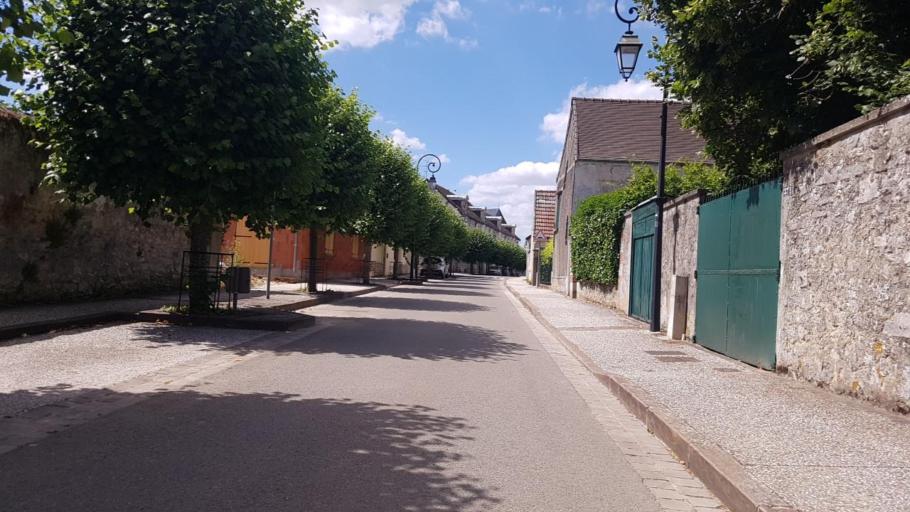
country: FR
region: Ile-de-France
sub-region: Departement de Seine-et-Marne
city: Moussy-le-Vieux
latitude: 49.0447
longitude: 2.6268
